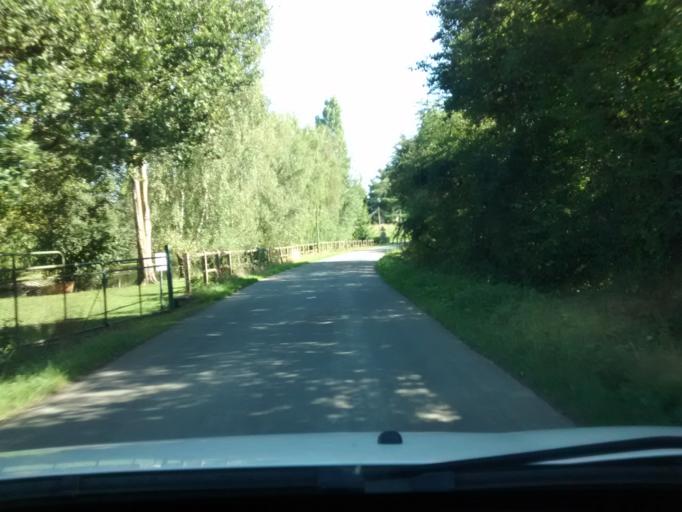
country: FR
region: Brittany
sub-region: Departement d'Ille-et-Vilaine
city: Chantepie
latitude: 48.0906
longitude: -1.5840
